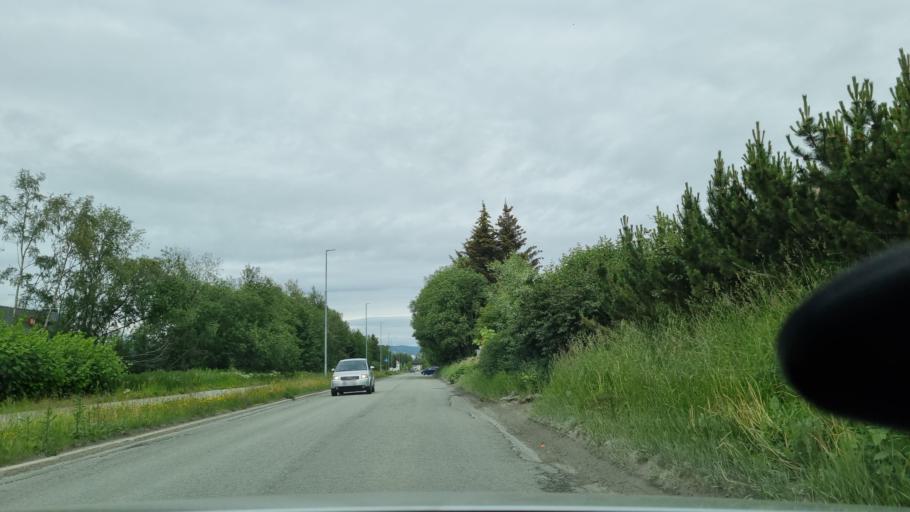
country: NO
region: Sor-Trondelag
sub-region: Trondheim
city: Trondheim
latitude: 63.3427
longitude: 10.3606
